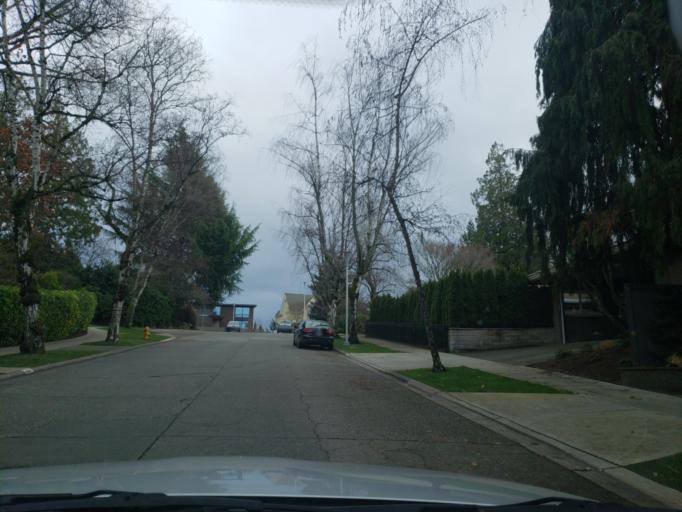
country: US
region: Washington
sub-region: King County
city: Medina
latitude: 47.6522
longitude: -122.2788
